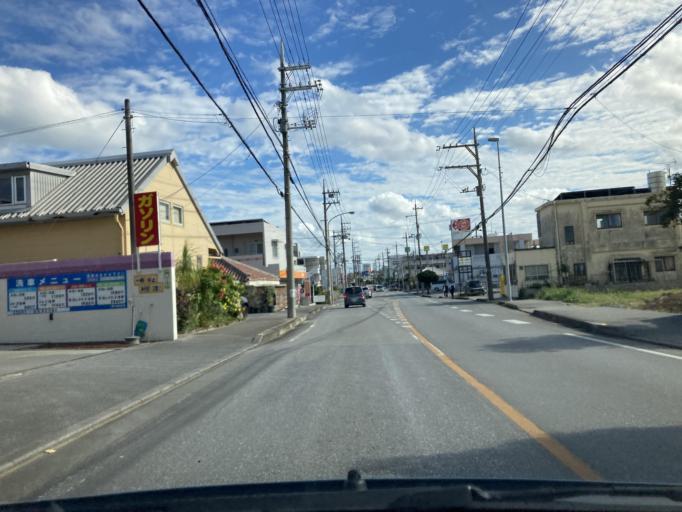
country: JP
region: Okinawa
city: Ishikawa
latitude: 26.4143
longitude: 127.8232
